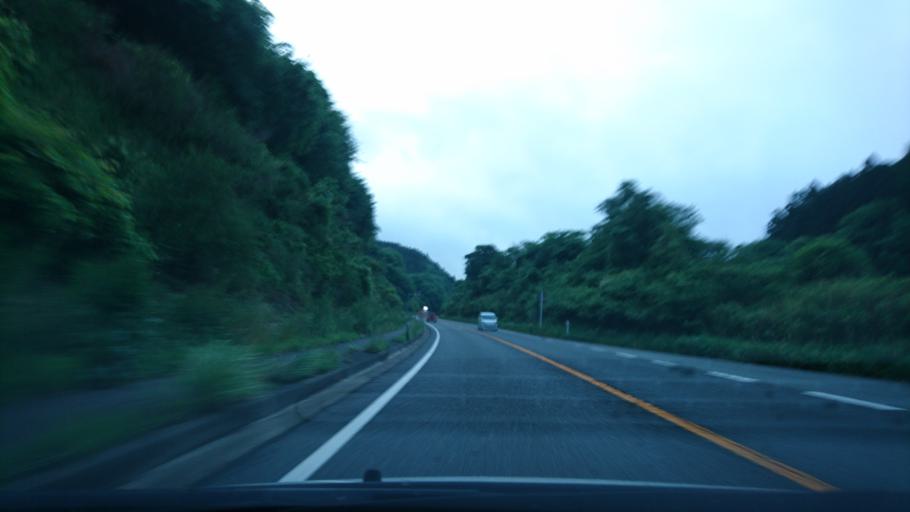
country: JP
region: Iwate
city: Ichinoseki
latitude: 38.8990
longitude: 141.1137
